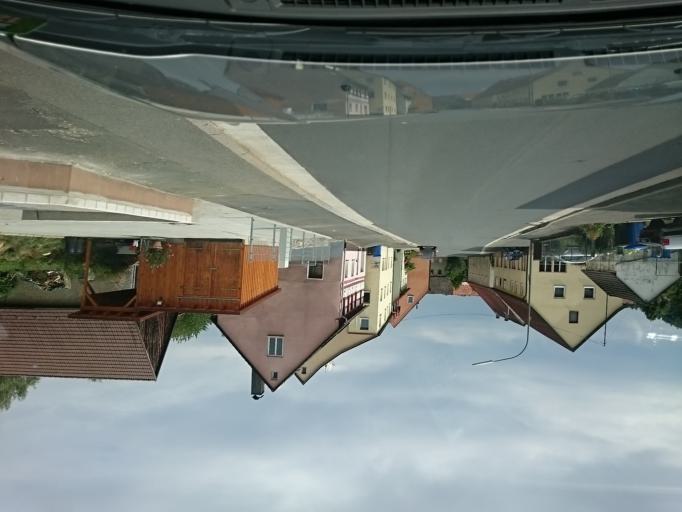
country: DE
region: Bavaria
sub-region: Regierungsbezirk Mittelfranken
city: Velden
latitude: 49.6496
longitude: 11.4701
